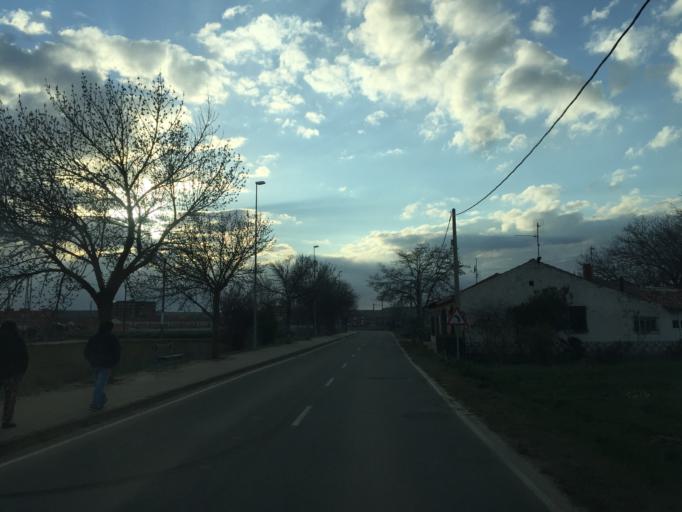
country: ES
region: Castille and Leon
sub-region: Provincia de Palencia
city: Venta de Banos
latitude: 41.9209
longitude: -4.4816
